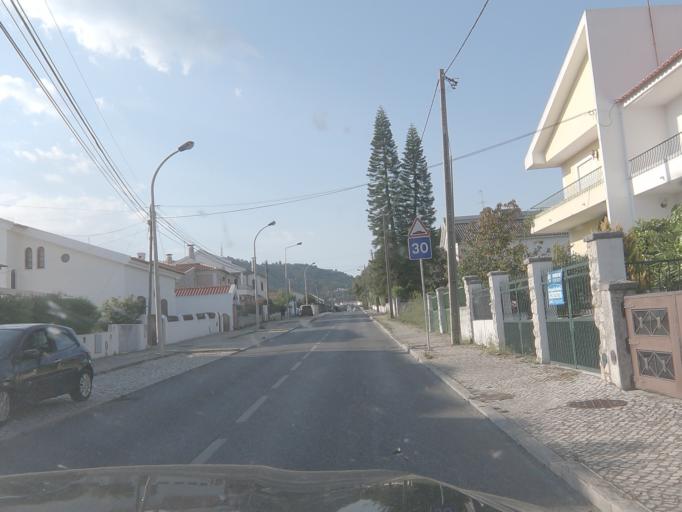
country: PT
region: Setubal
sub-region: Setubal
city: Setubal
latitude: 38.5423
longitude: -8.8980
